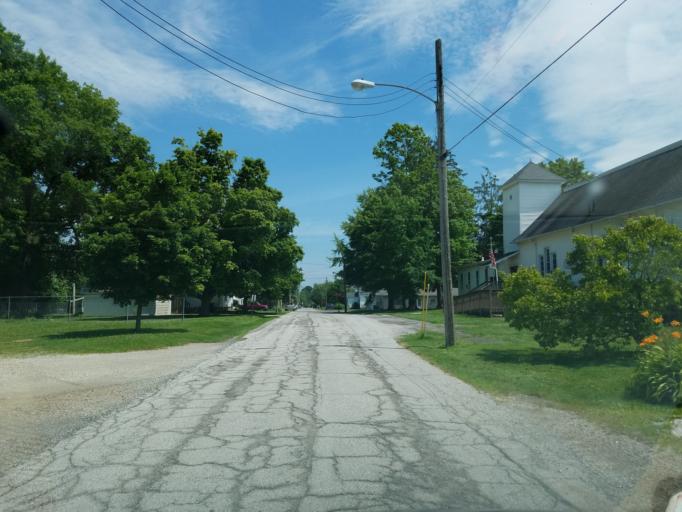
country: US
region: Ohio
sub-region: Ashland County
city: Ashland
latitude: 40.8759
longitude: -82.3253
